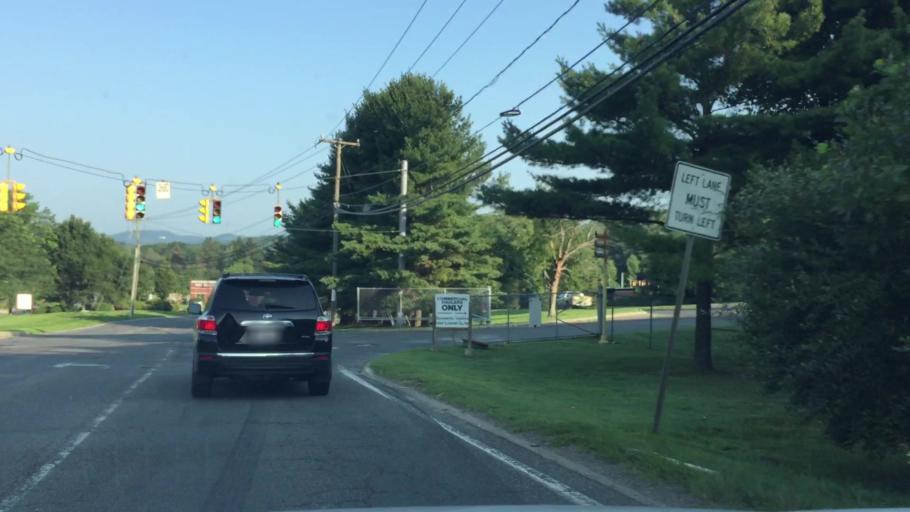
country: US
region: Massachusetts
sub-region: Berkshire County
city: Dalton
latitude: 42.4675
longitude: -73.1945
